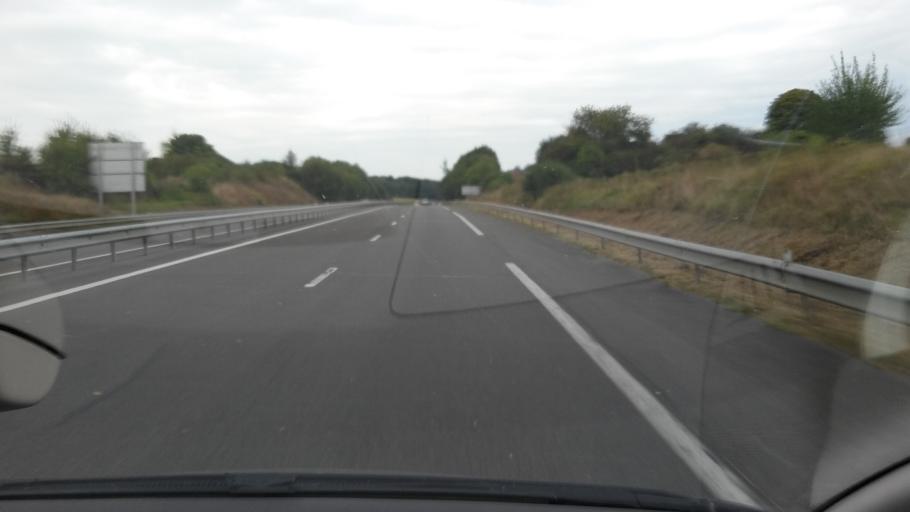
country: FR
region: Champagne-Ardenne
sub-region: Departement des Ardennes
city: La Francheville
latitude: 49.6527
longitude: 4.6341
